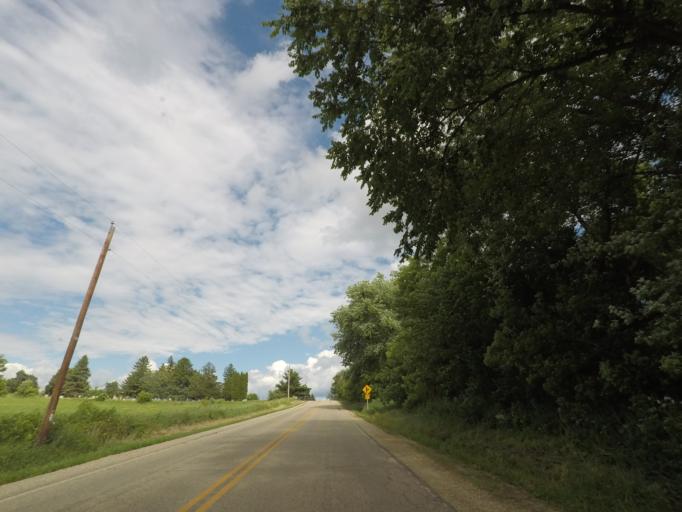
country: US
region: Wisconsin
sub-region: Rock County
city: Orfordville
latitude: 42.7092
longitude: -89.1837
